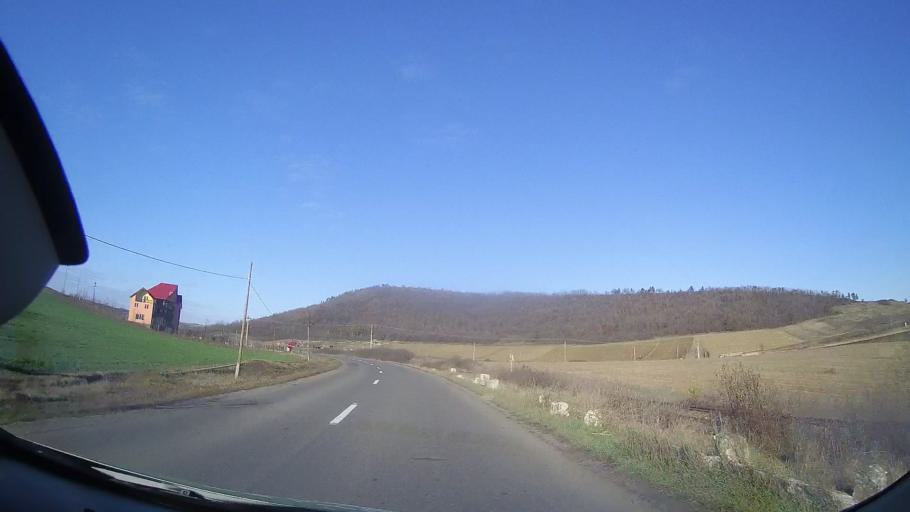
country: RO
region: Mures
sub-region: Comuna Mihesu de Campie
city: Mihesu de Campie
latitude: 46.6688
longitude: 24.1731
